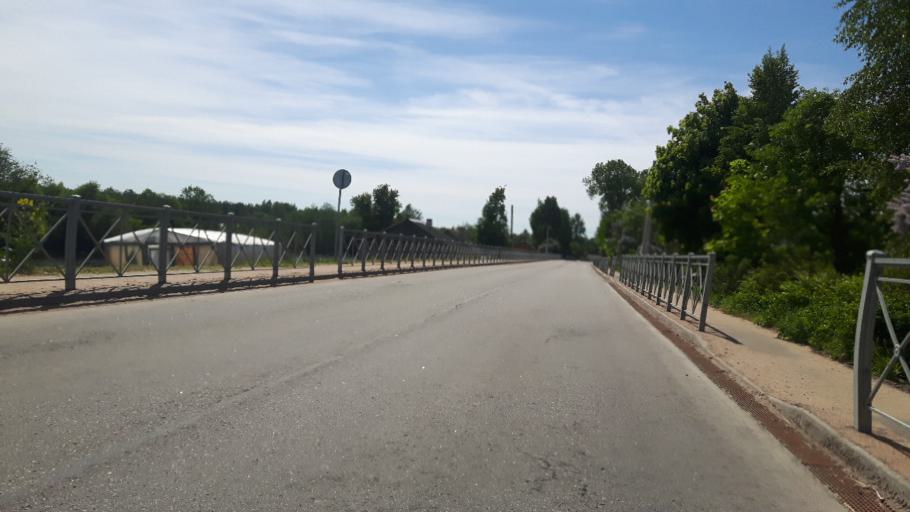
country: RU
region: Leningrad
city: Ust'-Luga
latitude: 59.5855
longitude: 28.1915
